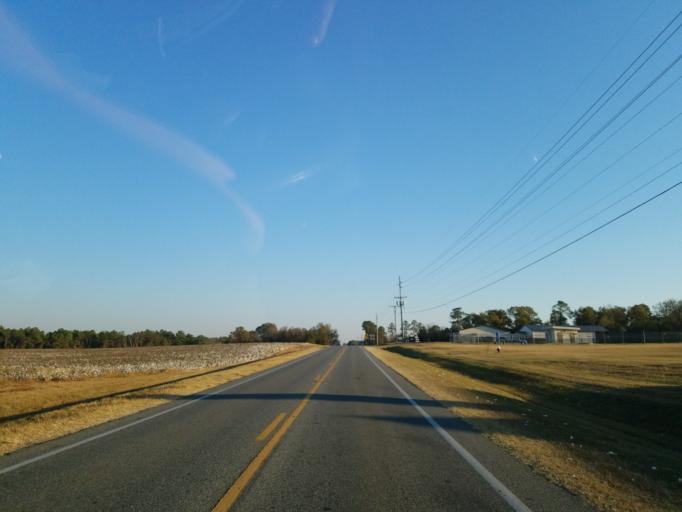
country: US
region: Georgia
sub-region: Crisp County
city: Cordele
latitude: 31.9452
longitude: -83.7411
